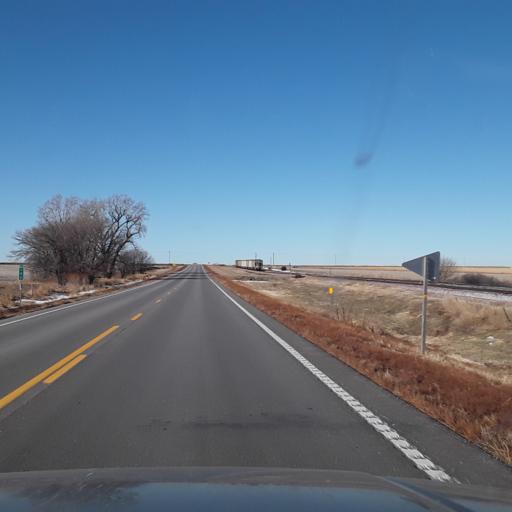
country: US
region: Nebraska
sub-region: Phelps County
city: Holdrege
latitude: 40.4858
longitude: -99.5249
